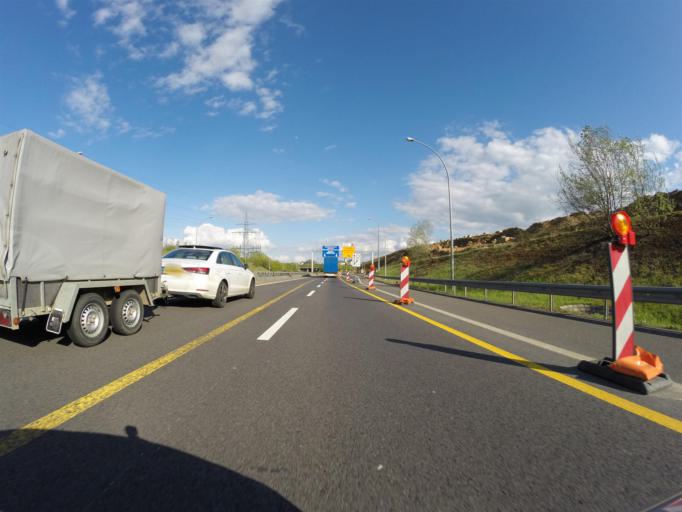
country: LU
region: Luxembourg
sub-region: Canton d'Esch-sur-Alzette
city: Frisange
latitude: 49.5090
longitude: 6.1843
